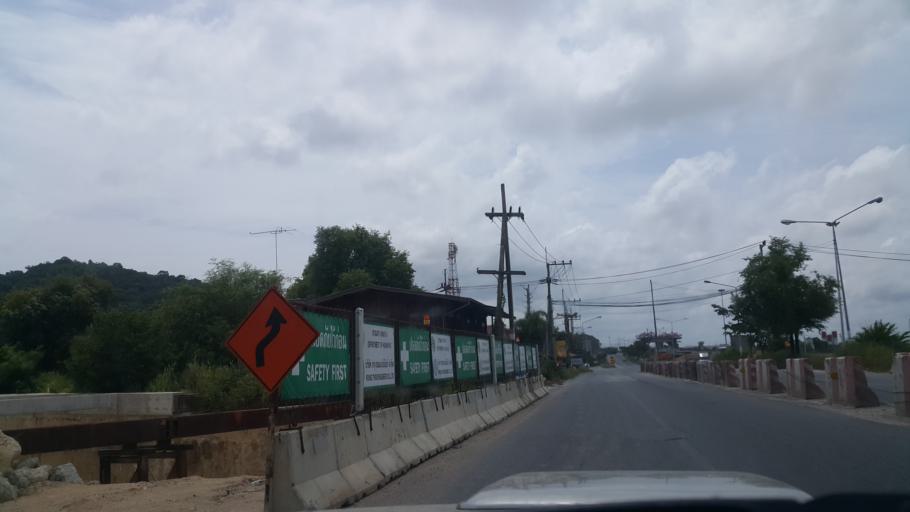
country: TH
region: Rayong
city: Ban Chang
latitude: 12.7098
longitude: 101.0273
